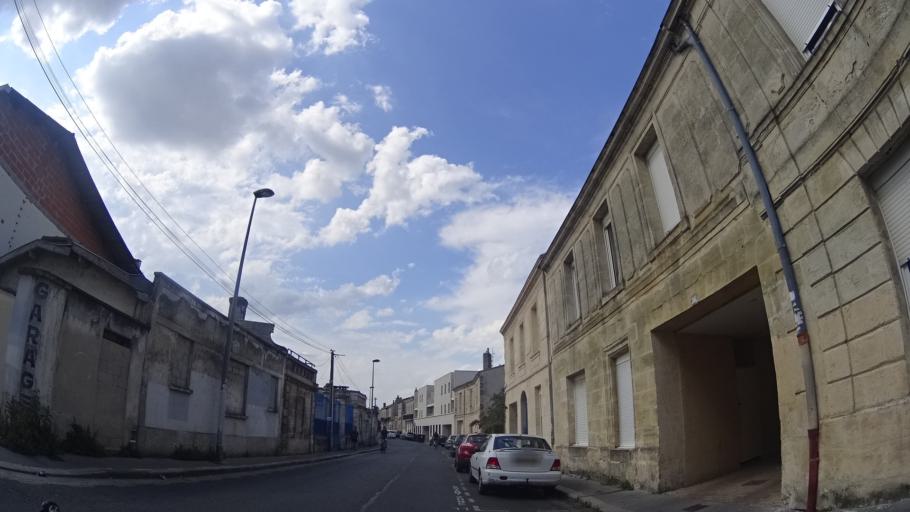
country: FR
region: Aquitaine
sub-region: Departement de la Gironde
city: Bordeaux
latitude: 44.8239
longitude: -0.5660
